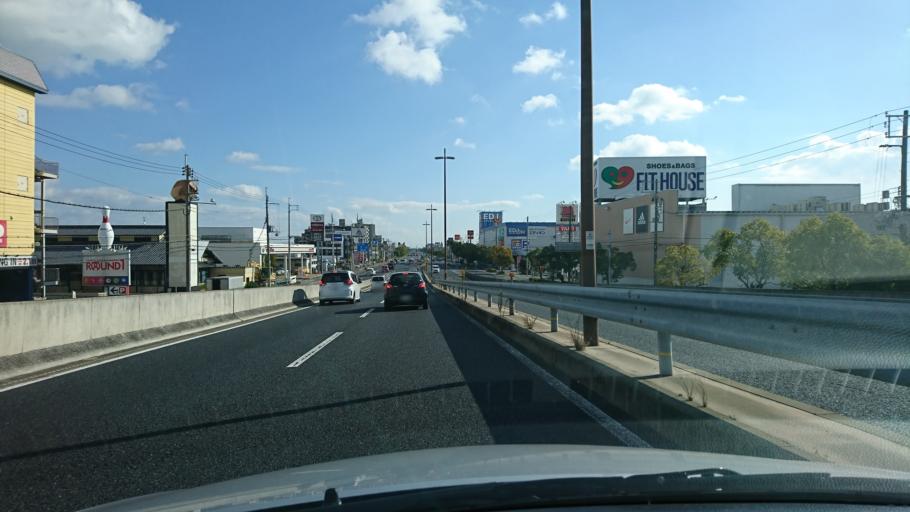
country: JP
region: Hyogo
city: Kakogawacho-honmachi
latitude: 34.7469
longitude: 134.8363
